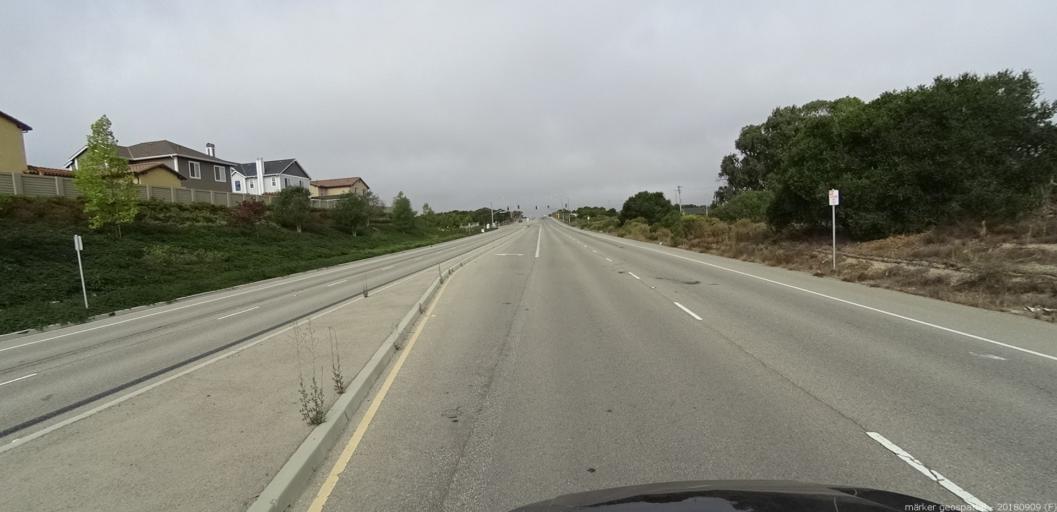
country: US
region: California
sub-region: Monterey County
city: Marina
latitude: 36.6588
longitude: -121.7397
